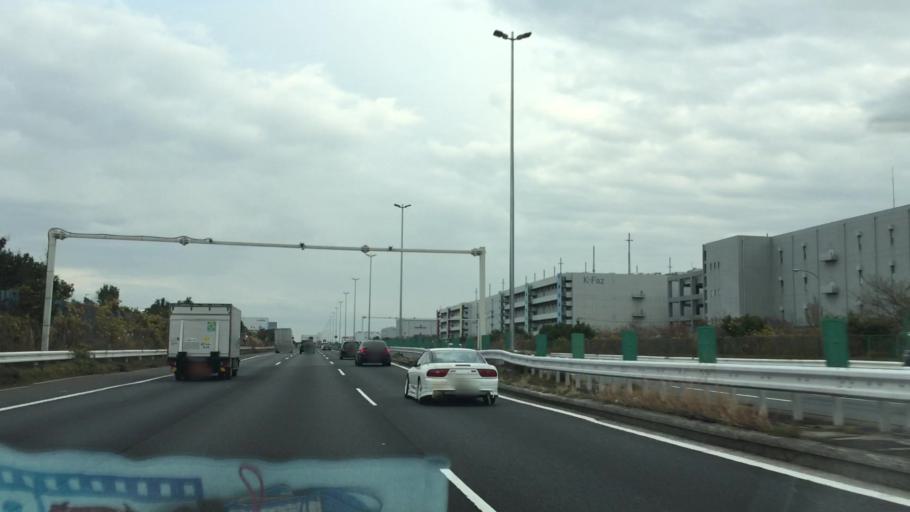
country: JP
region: Kanagawa
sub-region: Kawasaki-shi
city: Kawasaki
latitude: 35.4932
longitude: 139.7469
